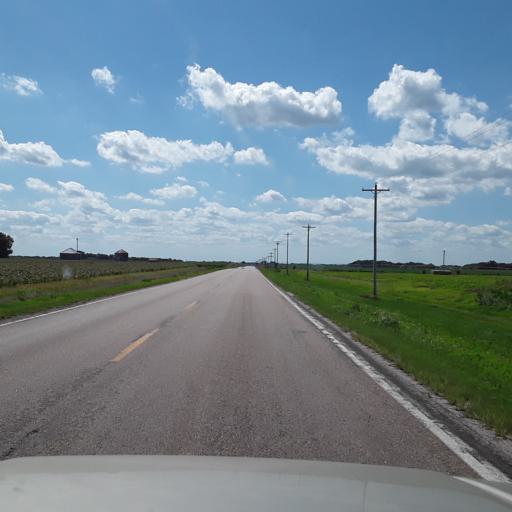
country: US
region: Nebraska
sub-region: Merrick County
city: Central City
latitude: 41.1911
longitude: -98.0362
